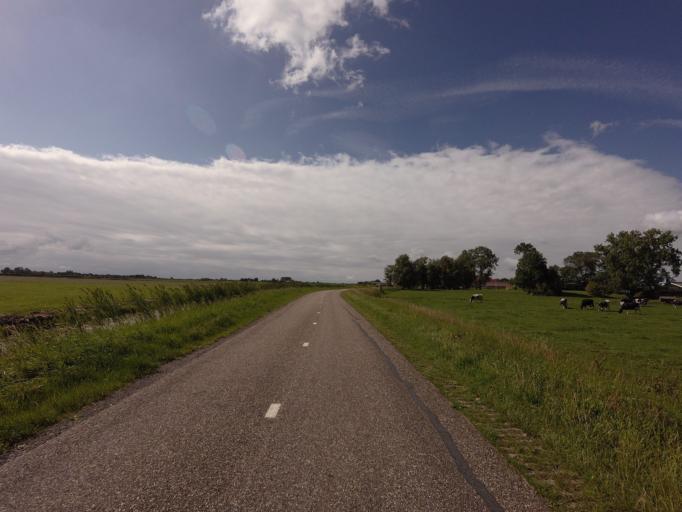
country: NL
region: Friesland
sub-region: Sudwest Fryslan
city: IJlst
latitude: 53.0259
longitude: 5.5860
